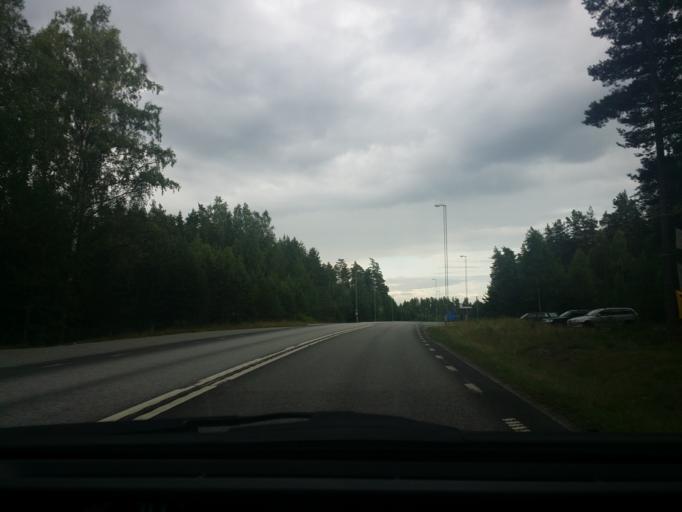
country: SE
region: OErebro
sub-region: Nora Kommun
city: Nora
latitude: 59.4730
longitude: 15.1268
